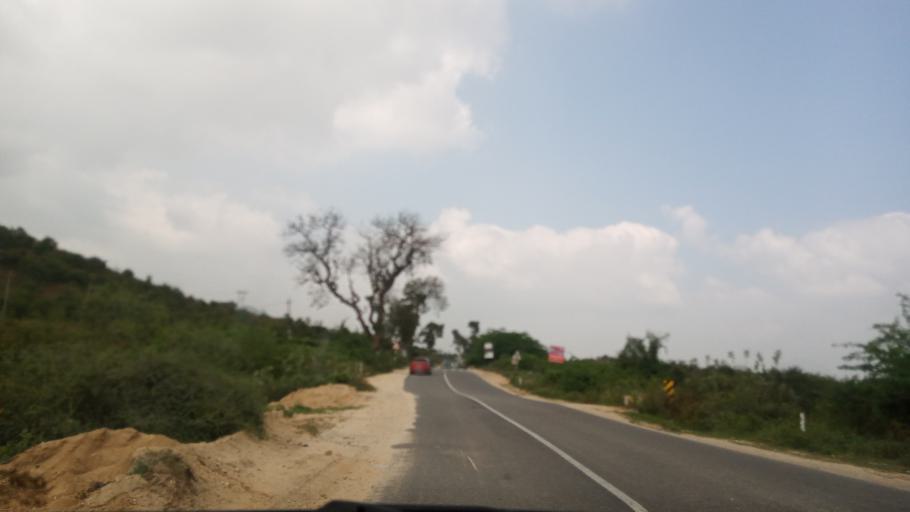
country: IN
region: Andhra Pradesh
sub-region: Chittoor
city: Madanapalle
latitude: 13.5881
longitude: 78.5255
